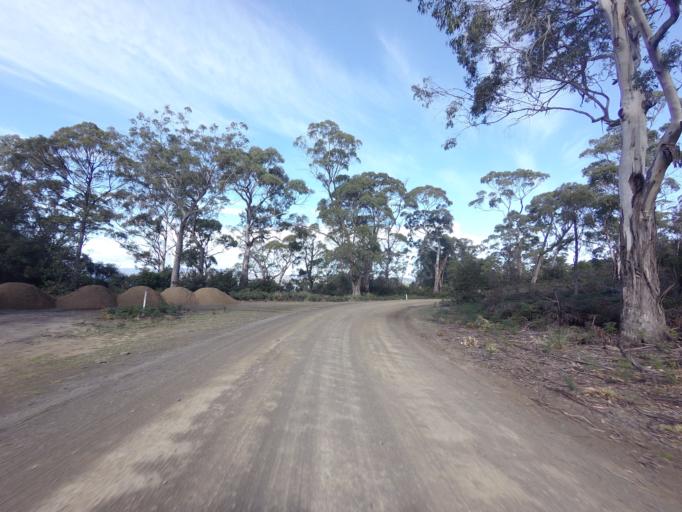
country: AU
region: Tasmania
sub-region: Clarence
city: Sandford
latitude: -42.9901
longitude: 147.7145
